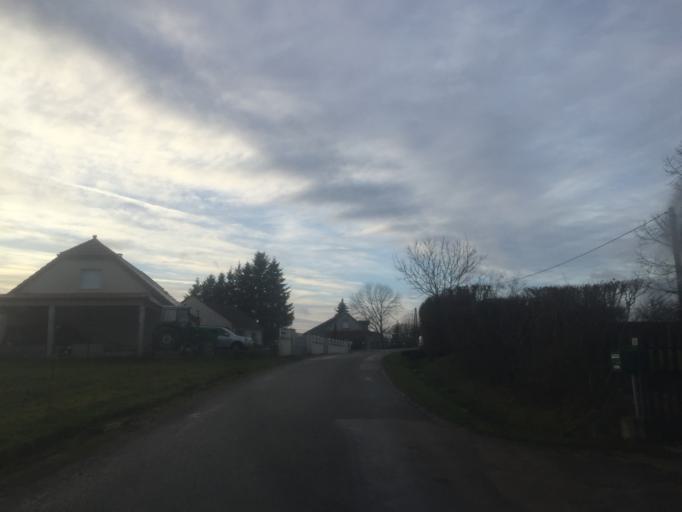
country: FR
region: Franche-Comte
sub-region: Departement du Jura
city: Orchamps
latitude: 47.1283
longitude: 5.6716
